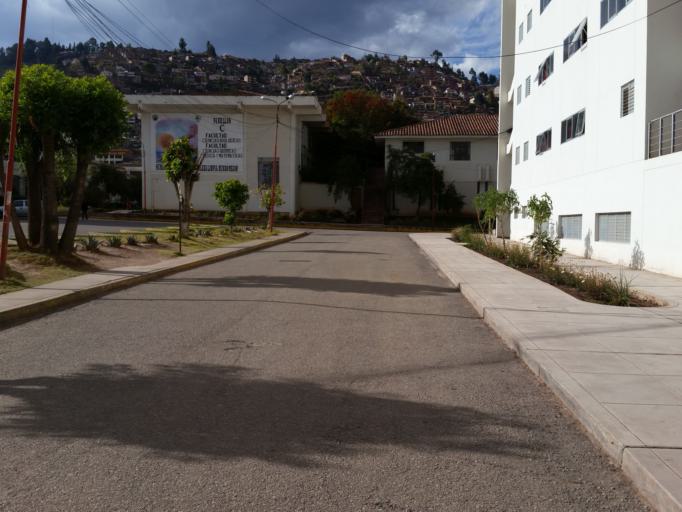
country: PE
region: Cusco
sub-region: Provincia de Cusco
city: Cusco
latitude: -13.5228
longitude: -71.9598
